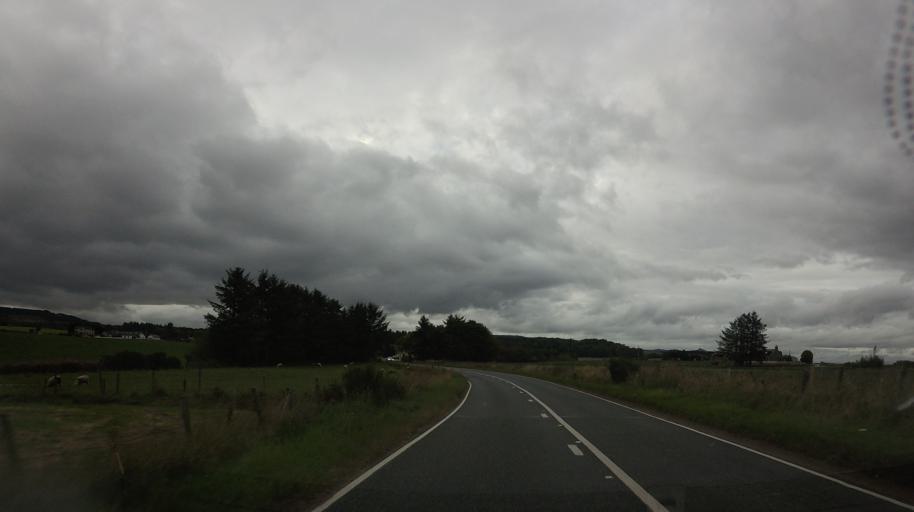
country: GB
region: Scotland
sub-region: Aberdeenshire
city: Kemnay
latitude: 57.1818
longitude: -2.5366
